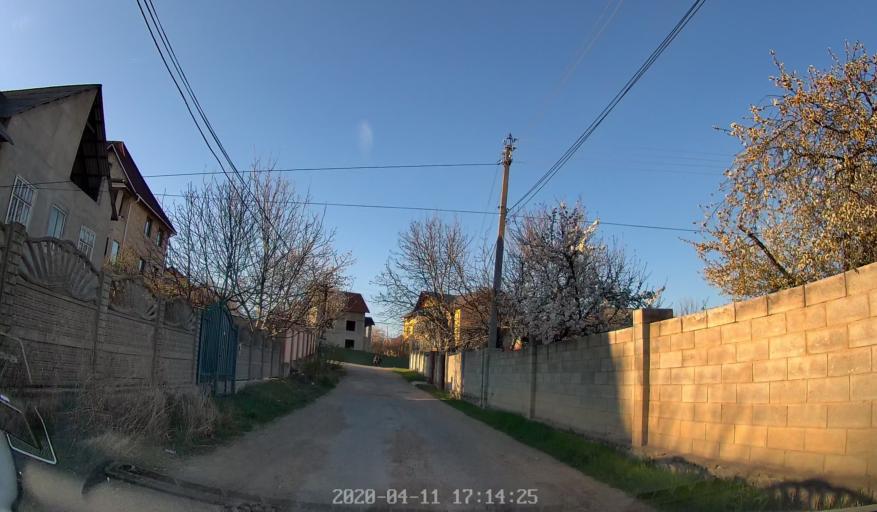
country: MD
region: Chisinau
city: Vatra
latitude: 47.0350
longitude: 28.7571
